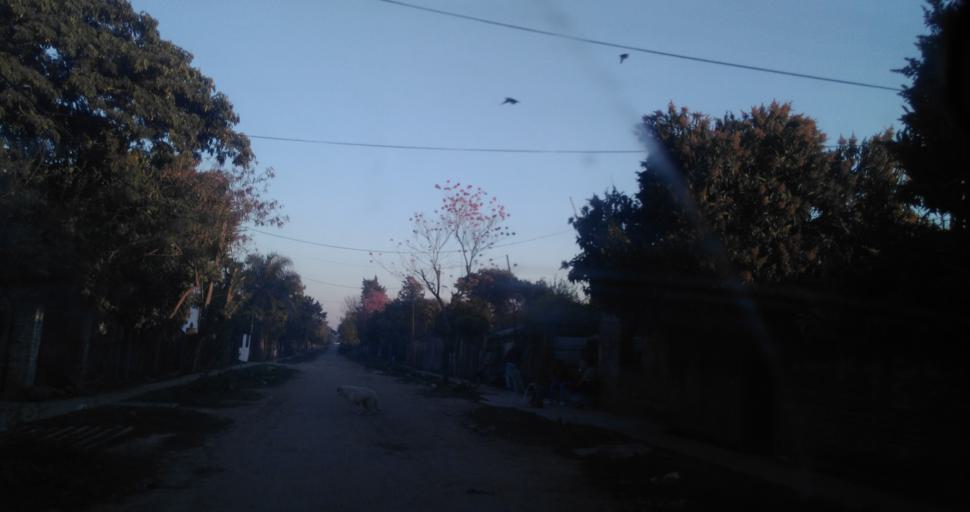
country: AR
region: Chaco
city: Fontana
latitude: -27.4274
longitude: -59.0216
